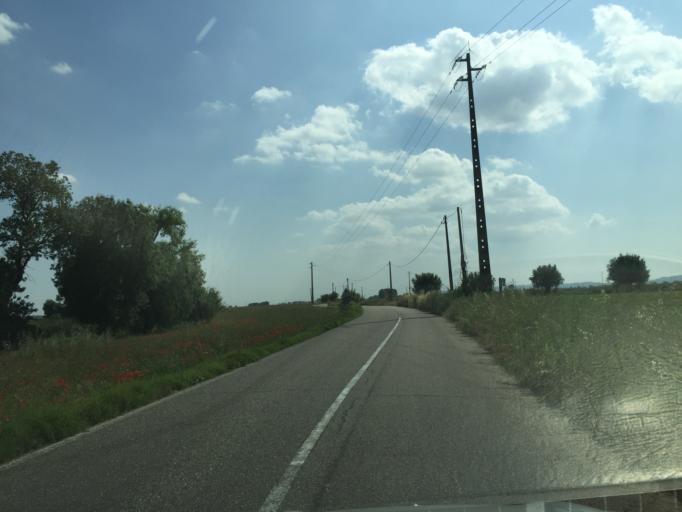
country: PT
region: Santarem
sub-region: Alpiarca
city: Alpiarca
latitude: 39.2935
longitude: -8.5823
